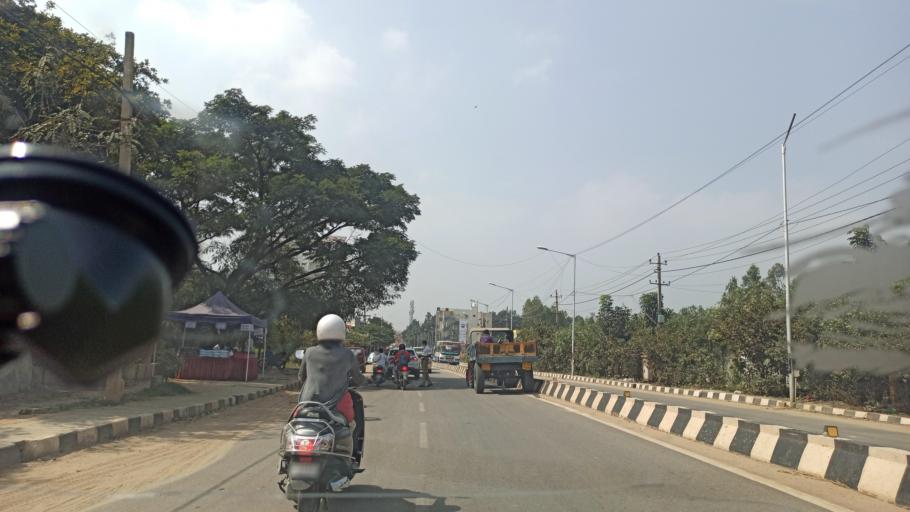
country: IN
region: Karnataka
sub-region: Bangalore Urban
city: Yelahanka
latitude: 13.1044
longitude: 77.6121
